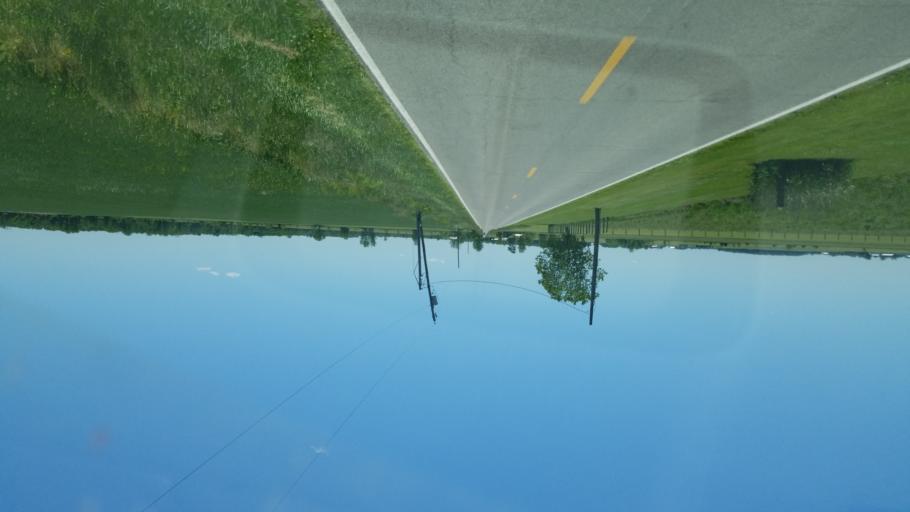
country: US
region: Indiana
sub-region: Randolph County
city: Union City
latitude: 40.3005
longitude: -84.8037
